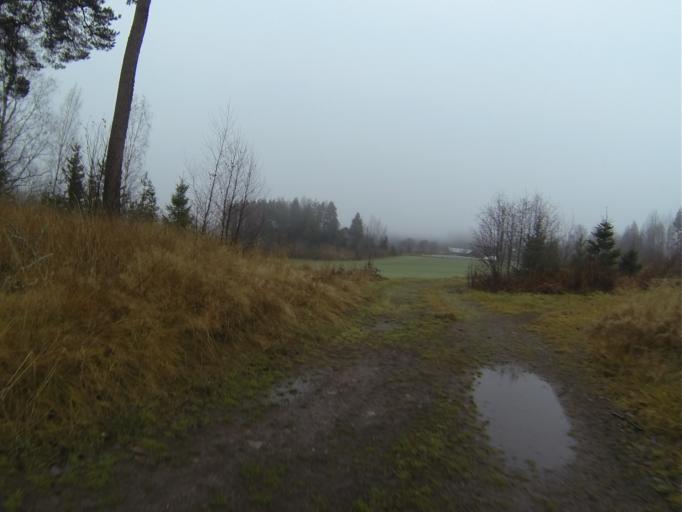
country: FI
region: Varsinais-Suomi
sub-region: Salo
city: Halikko
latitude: 60.4096
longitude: 22.9591
